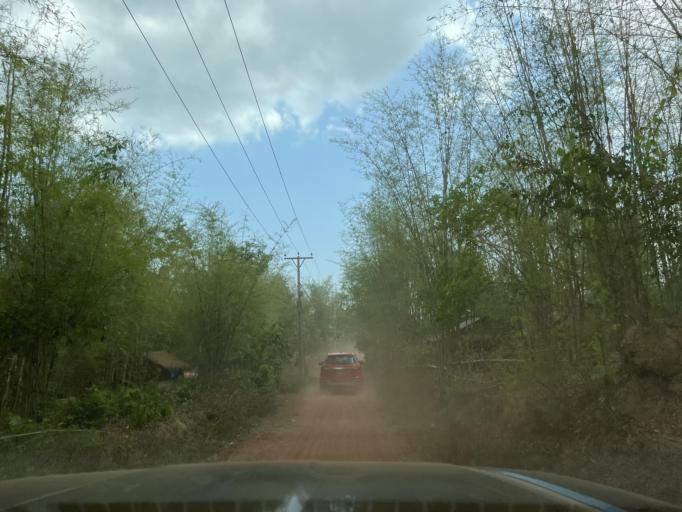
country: MM
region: Yangon
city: Twante
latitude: 16.5748
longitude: 95.9262
